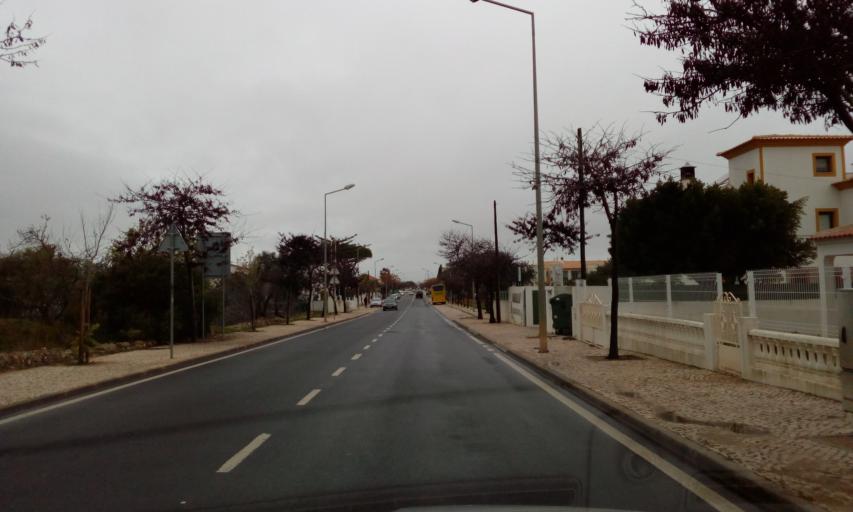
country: PT
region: Faro
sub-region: Albufeira
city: Ferreiras
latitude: 37.1245
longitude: -8.2244
